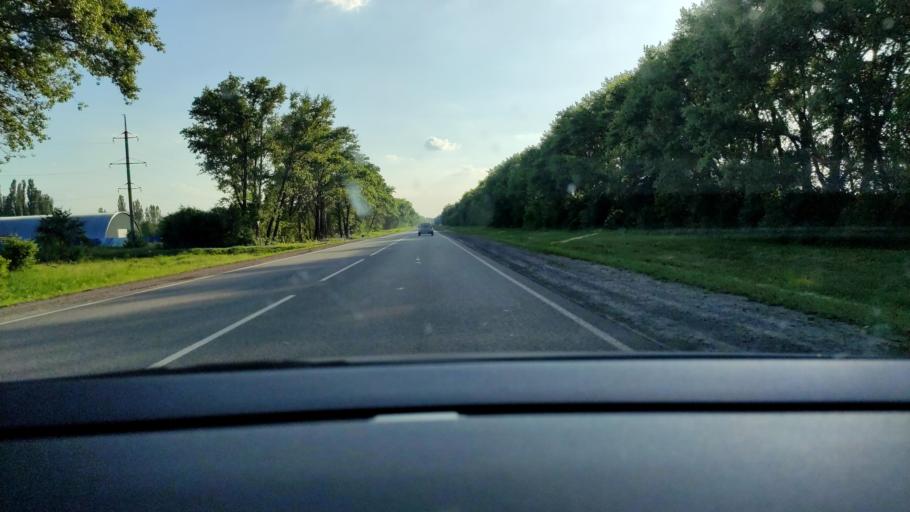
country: RU
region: Voronezj
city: Kashirskoye
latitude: 51.4653
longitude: 39.8555
